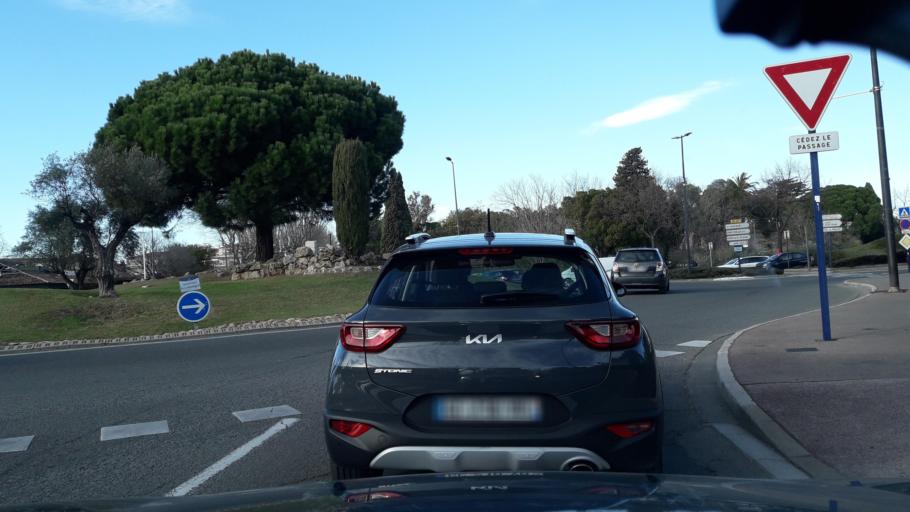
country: FR
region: Provence-Alpes-Cote d'Azur
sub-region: Departement du Var
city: Frejus
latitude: 43.4276
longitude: 6.7369
